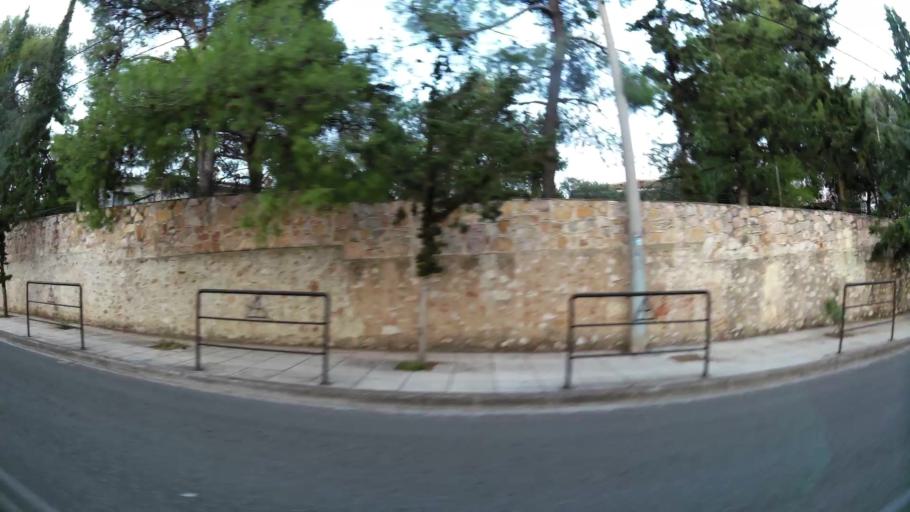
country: GR
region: Attica
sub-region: Nomarchia Athinas
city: Psychiko
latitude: 38.0162
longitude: 23.7787
